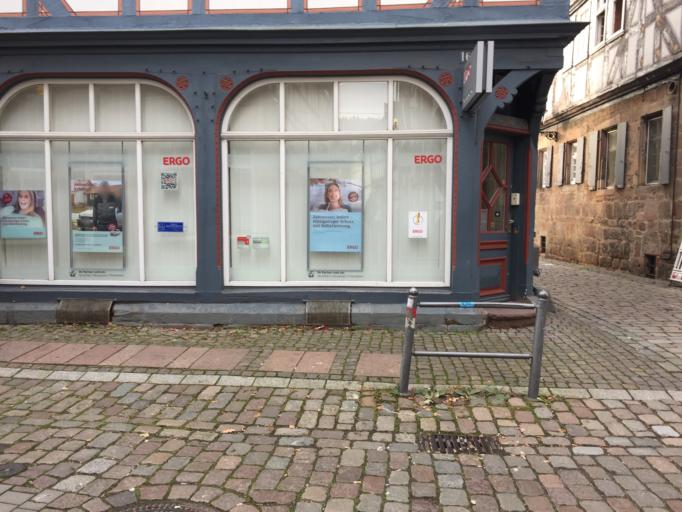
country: DE
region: Hesse
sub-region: Regierungsbezirk Giessen
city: Marburg an der Lahn
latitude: 50.8073
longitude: 8.7744
